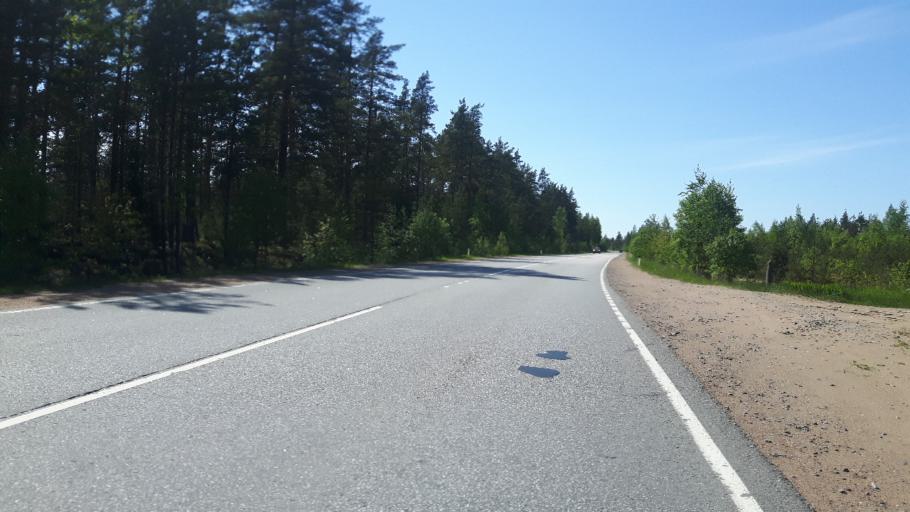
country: RU
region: Leningrad
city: Sista-Palkino
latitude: 59.7681
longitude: 28.7986
